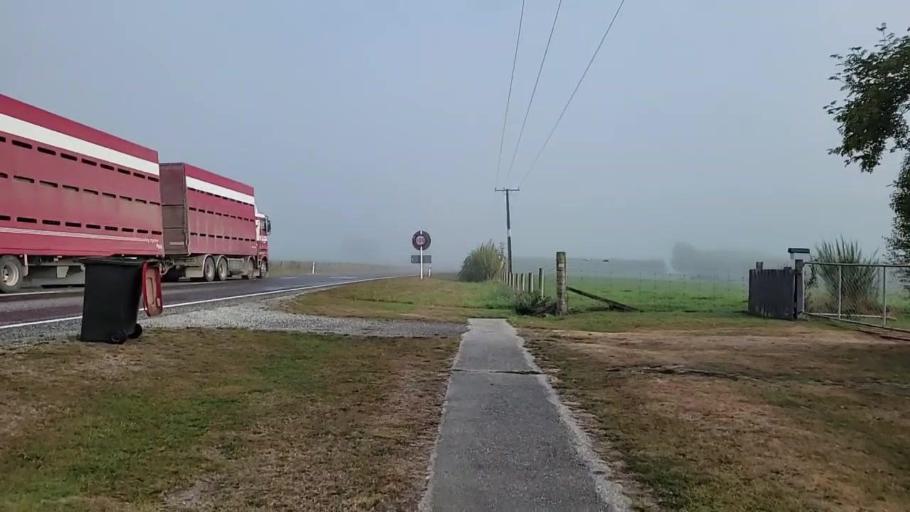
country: NZ
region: Southland
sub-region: Gore District
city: Gore
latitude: -45.6317
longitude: 169.3603
